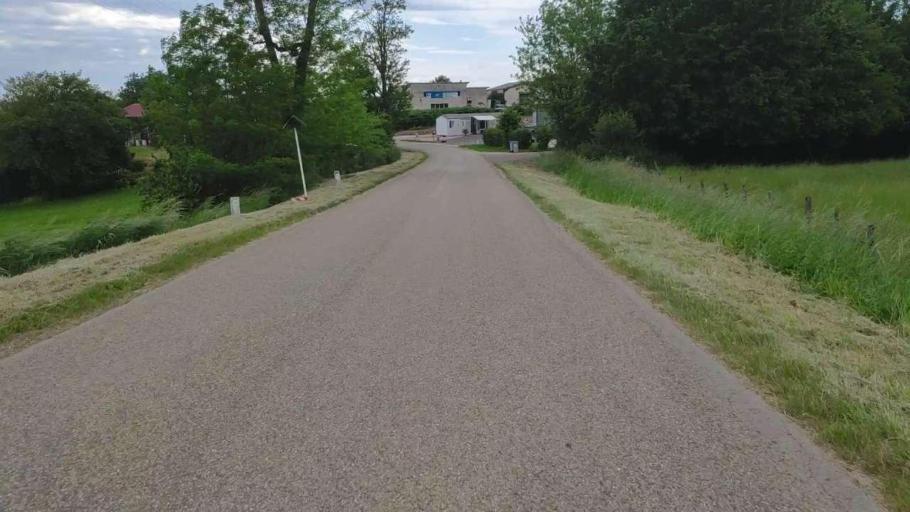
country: FR
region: Franche-Comte
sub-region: Departement du Jura
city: Bletterans
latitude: 46.7984
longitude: 5.5538
